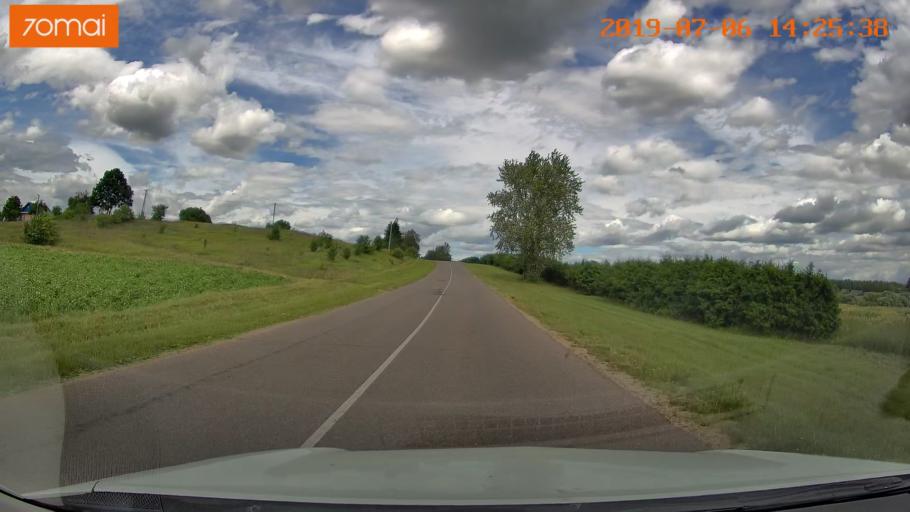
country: BY
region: Minsk
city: Ivyanyets
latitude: 53.9310
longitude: 26.7939
